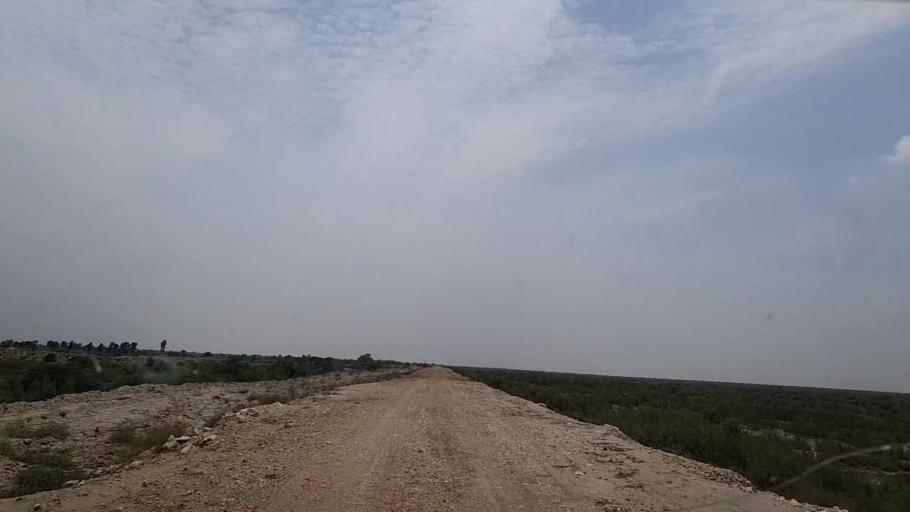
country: PK
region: Sindh
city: Phulji
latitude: 26.8628
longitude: 67.6394
